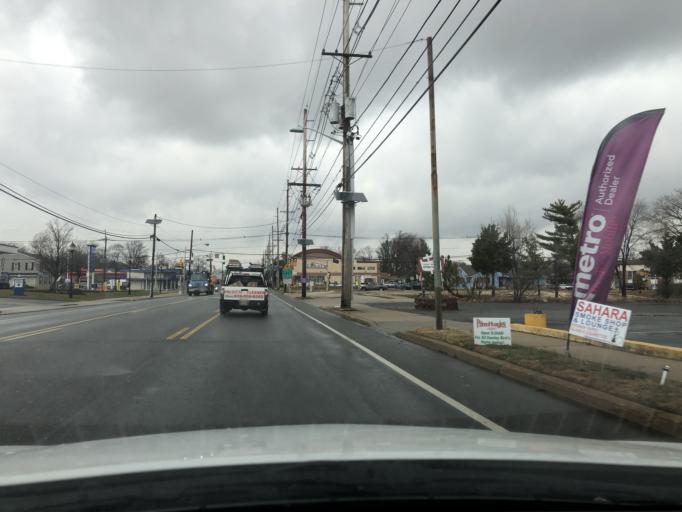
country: US
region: New Jersey
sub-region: Camden County
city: Bellmawr
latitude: 39.8656
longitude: -75.0790
